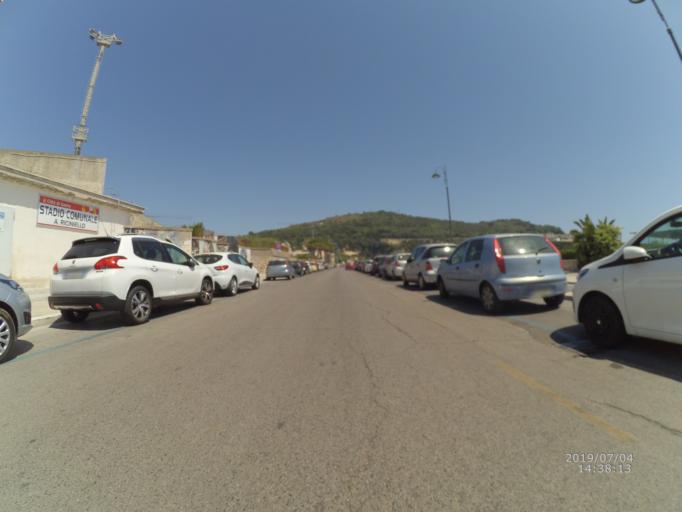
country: IT
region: Latium
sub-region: Provincia di Latina
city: Gaeta
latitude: 41.2108
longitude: 13.5661
